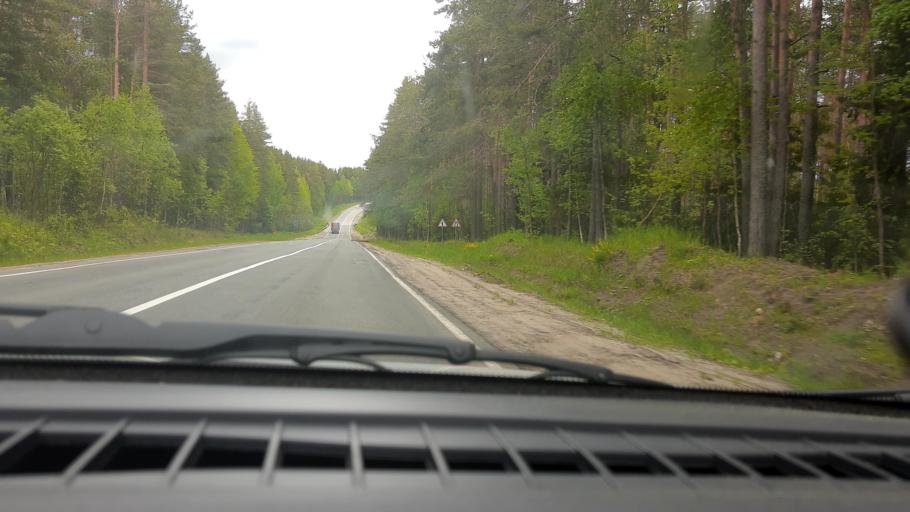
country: RU
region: Nizjnij Novgorod
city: Krasnyye Baki
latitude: 56.9911
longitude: 45.1156
